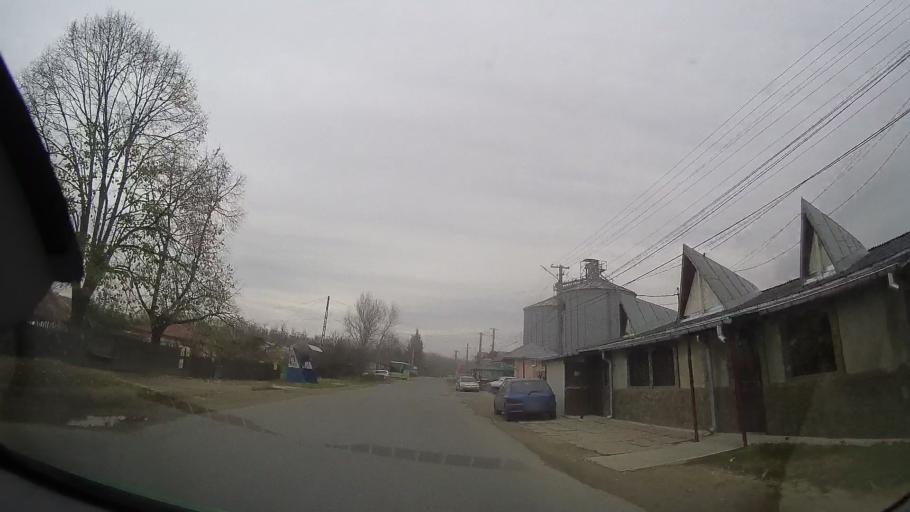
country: RO
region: Prahova
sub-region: Comuna Iordachianu
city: Iordacheanu
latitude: 45.0156
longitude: 26.2295
